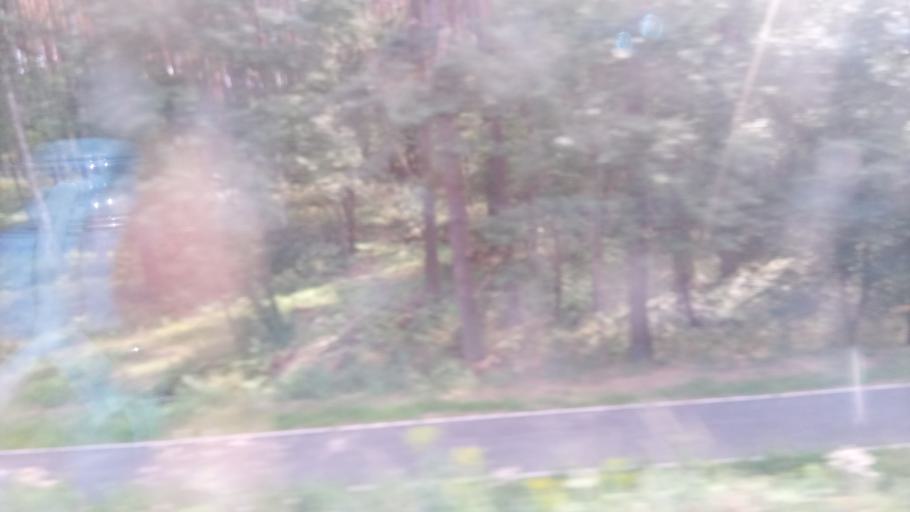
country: PL
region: Greater Poland Voivodeship
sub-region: Powiat pilski
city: Kaczory
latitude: 53.1111
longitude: 16.8531
